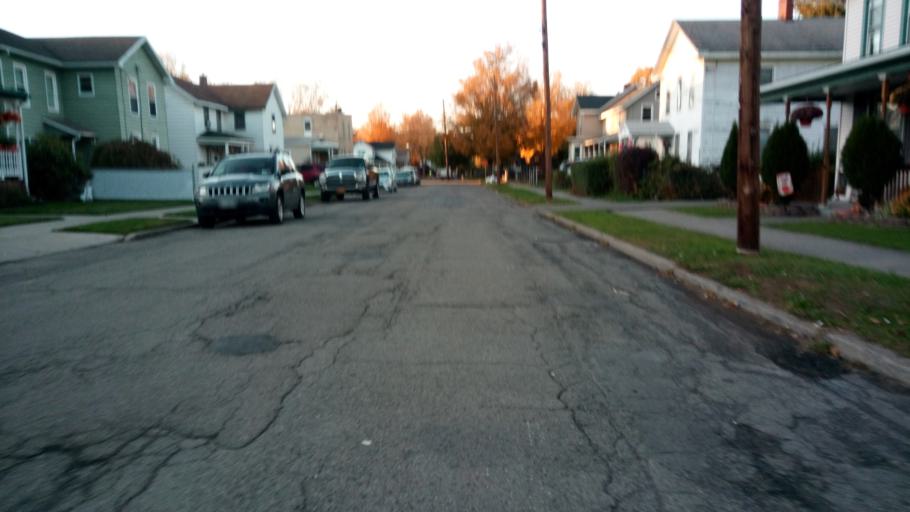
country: US
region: New York
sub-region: Chemung County
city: Elmira
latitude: 42.0748
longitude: -76.8092
